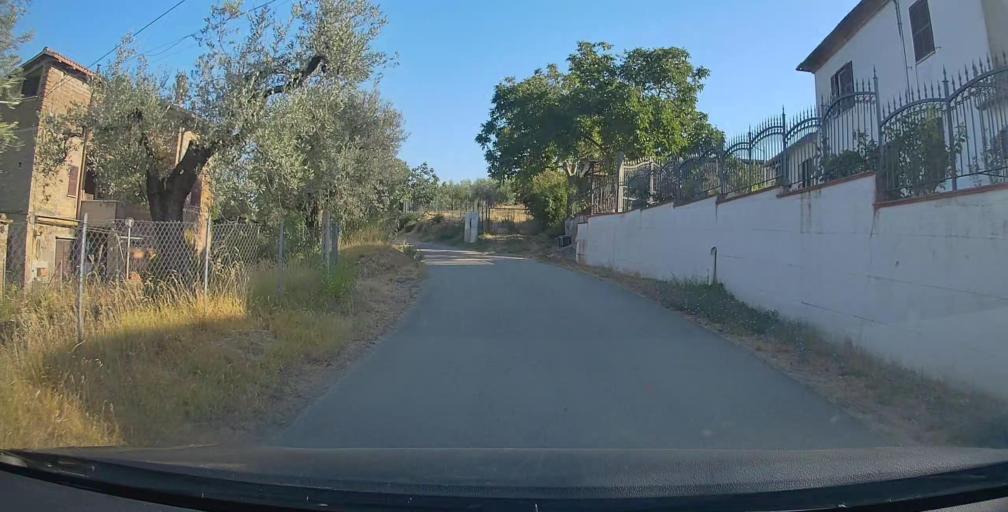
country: IT
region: Umbria
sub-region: Provincia di Terni
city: Calvi dell'Umbria
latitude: 42.3814
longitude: 12.5690
